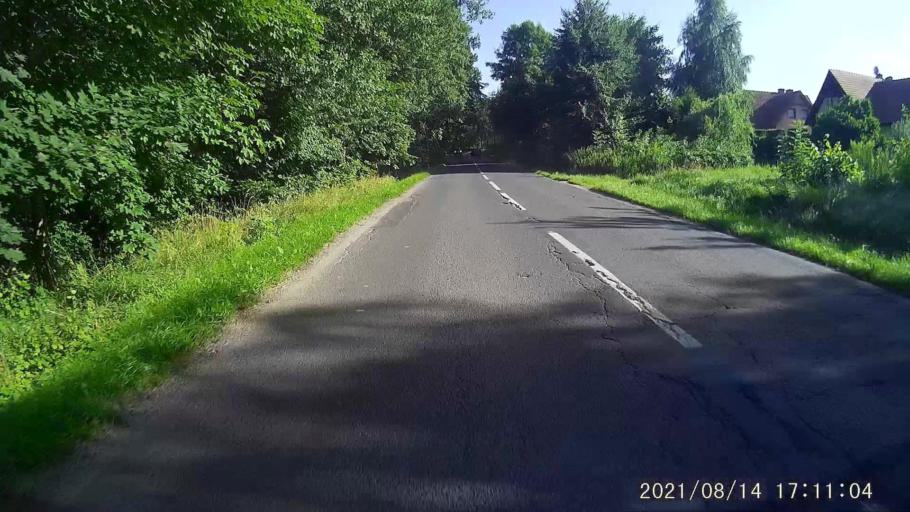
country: PL
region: Lower Silesian Voivodeship
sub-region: Powiat jeleniogorski
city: Myslakowice
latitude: 50.8310
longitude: 15.7921
